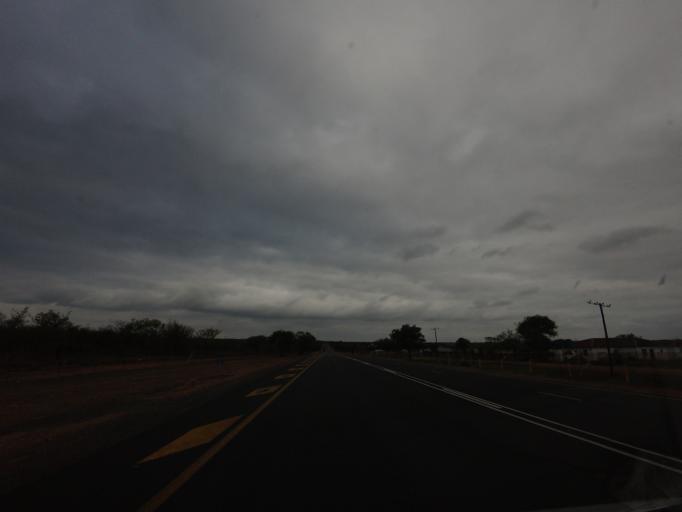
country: ZA
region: Mpumalanga
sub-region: Ehlanzeni District
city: Komatipoort
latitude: -25.4424
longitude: 31.6998
